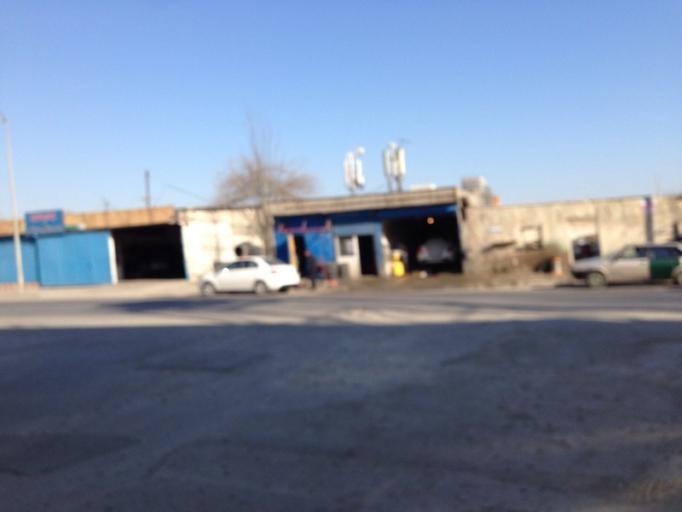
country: AZ
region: Baki
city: Baku
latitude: 40.4041
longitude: 49.8771
